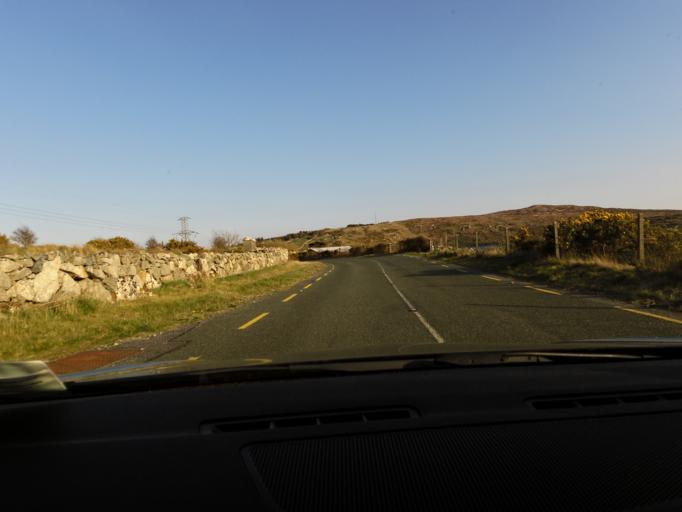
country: IE
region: Connaught
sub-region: County Galway
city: Oughterard
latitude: 53.3816
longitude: -9.5882
